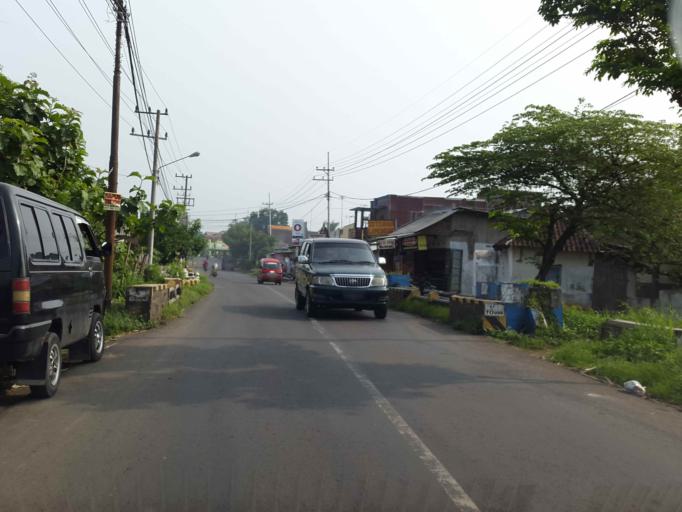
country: ID
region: East Java
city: Tamiajeng
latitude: -7.9561
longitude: 112.6997
